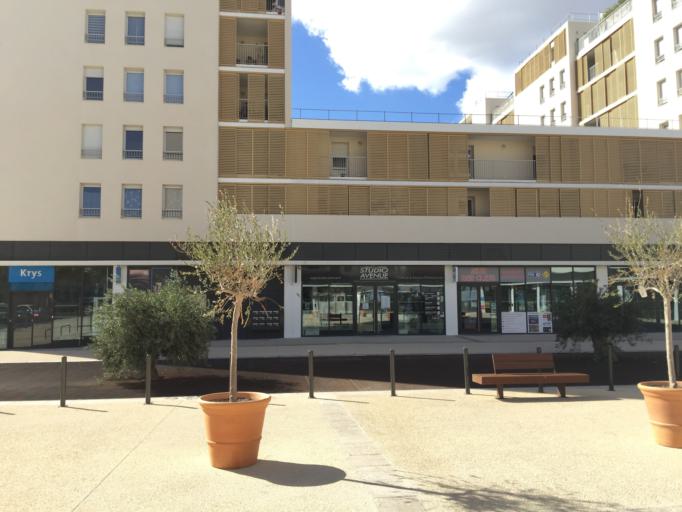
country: FR
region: Provence-Alpes-Cote d'Azur
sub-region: Departement des Bouches-du-Rhone
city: Marseille 11
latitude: 43.2843
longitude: 5.4351
